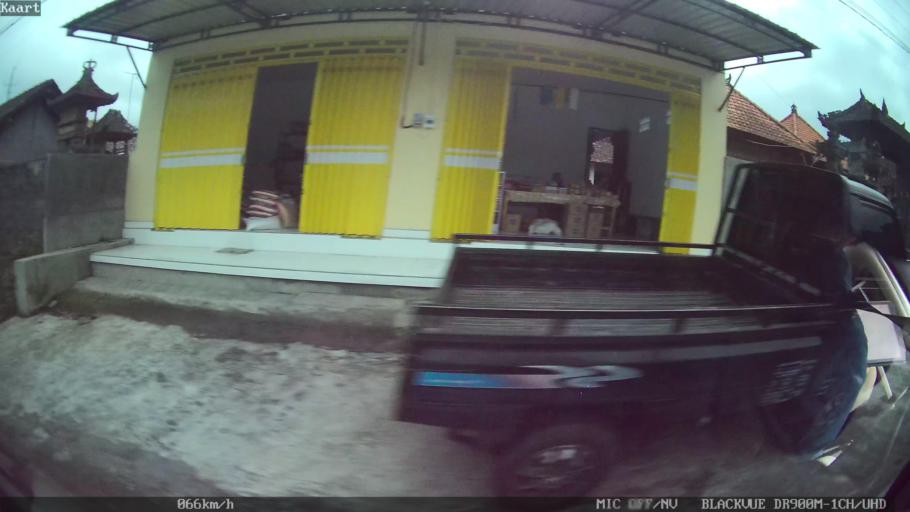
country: ID
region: Bali
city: Banjar Kubu
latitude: -8.4034
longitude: 115.4209
